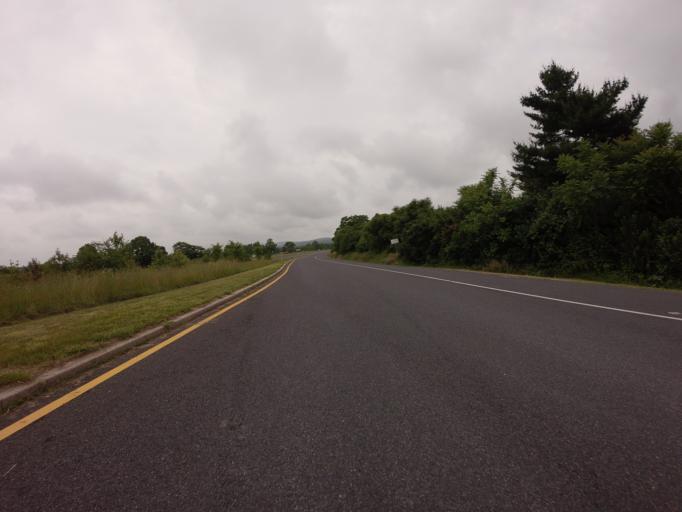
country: US
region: Maryland
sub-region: Frederick County
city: Ballenger Creek
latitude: 39.3773
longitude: -77.4766
